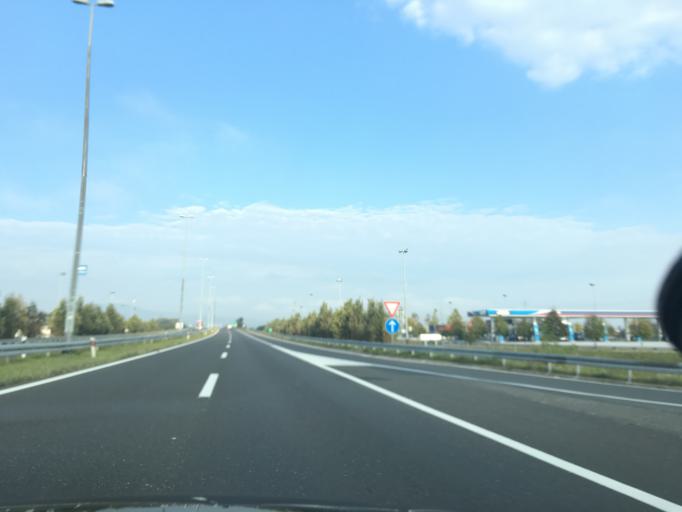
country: HR
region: Zagrebacka
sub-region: Grad Samobor
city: Samobor
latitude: 45.8257
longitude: 15.7400
